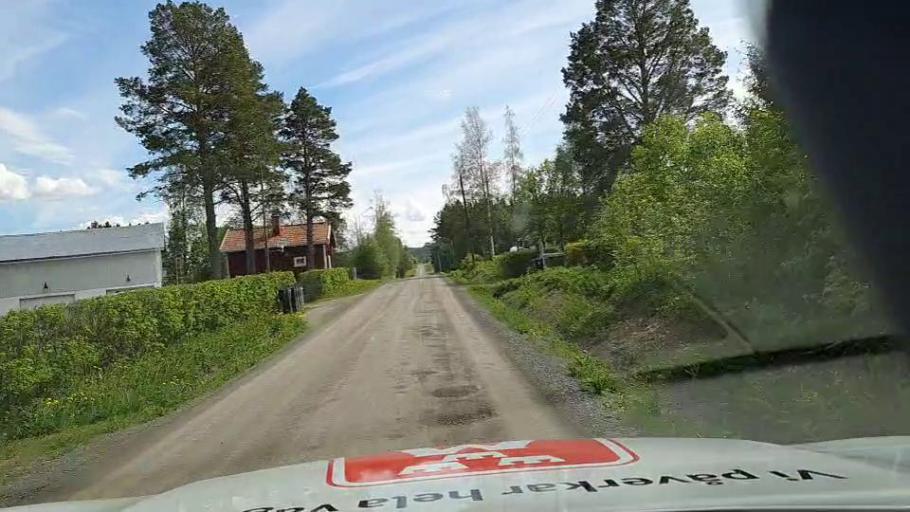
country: SE
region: Jaemtland
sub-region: OEstersunds Kommun
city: Brunflo
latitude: 62.9919
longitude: 14.8079
